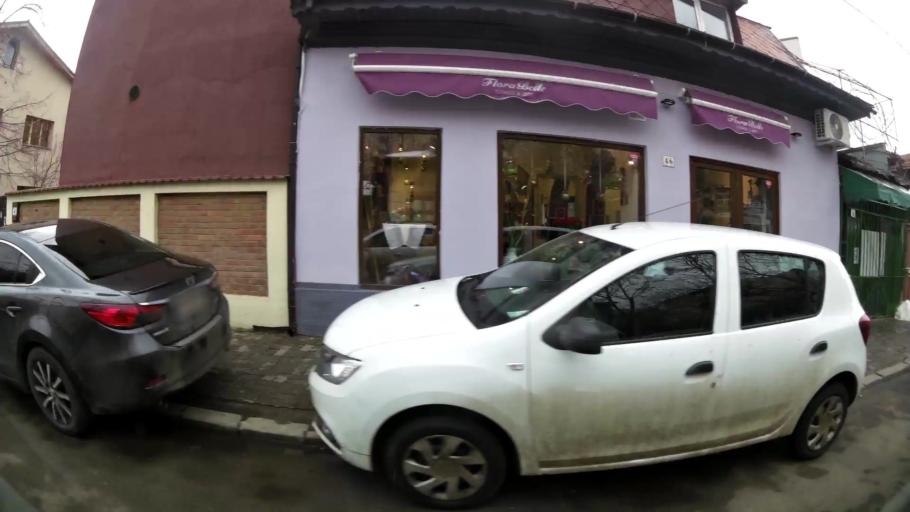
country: RO
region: Bucuresti
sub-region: Municipiul Bucuresti
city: Bucuresti
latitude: 44.4555
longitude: 26.0749
